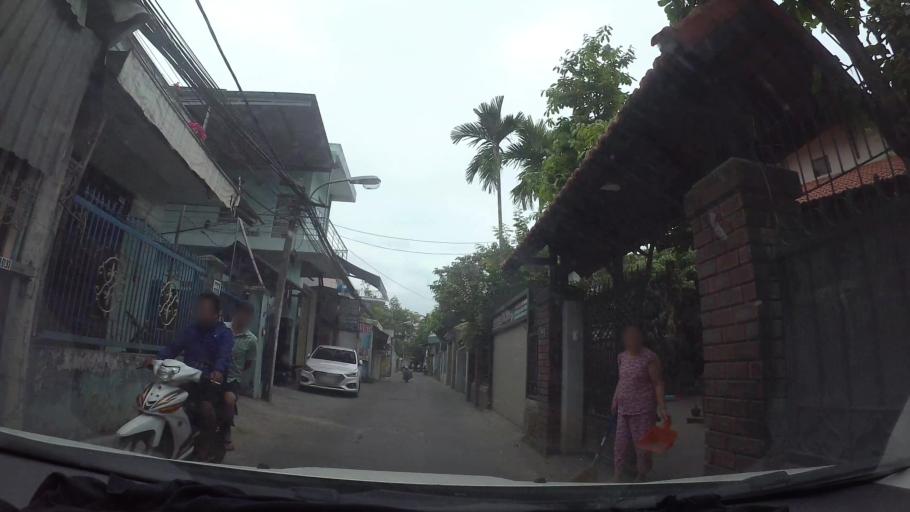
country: VN
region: Da Nang
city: Lien Chieu
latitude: 16.0659
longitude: 108.1524
